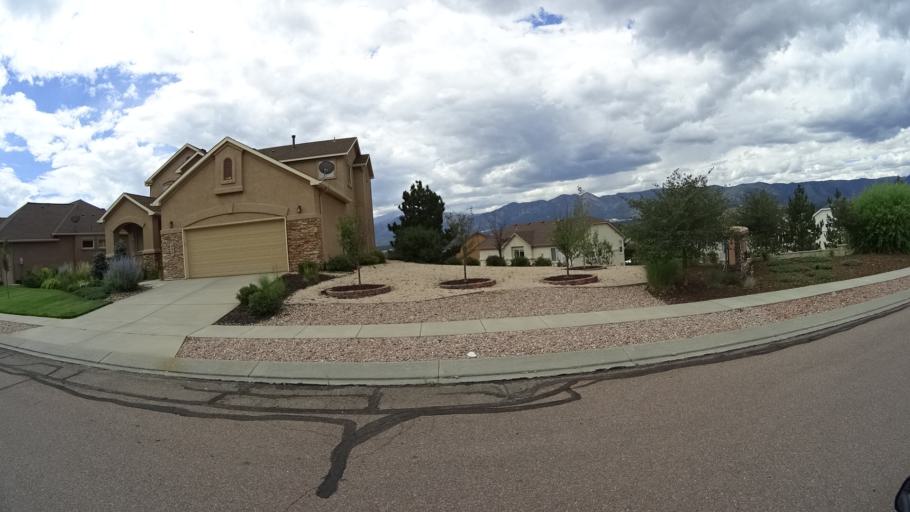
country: US
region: Colorado
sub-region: El Paso County
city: Gleneagle
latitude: 39.0306
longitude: -104.8146
